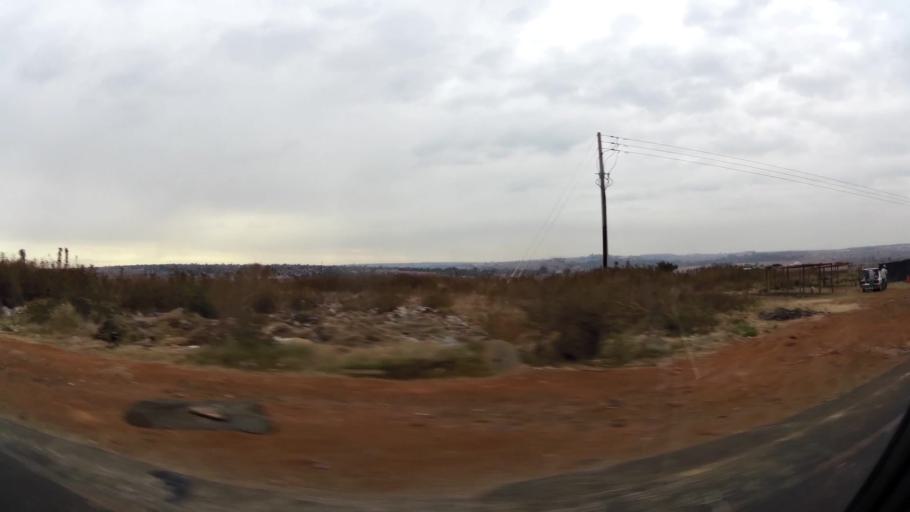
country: ZA
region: Gauteng
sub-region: City of Johannesburg Metropolitan Municipality
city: Roodepoort
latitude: -26.1699
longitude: 27.8078
